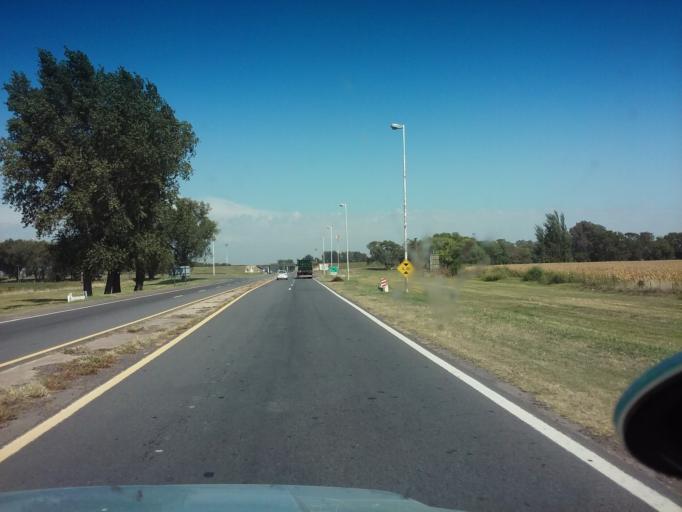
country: AR
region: Buenos Aires
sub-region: Partido de Nueve de Julio
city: Nueve de Julio
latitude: -35.4904
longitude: -60.8928
